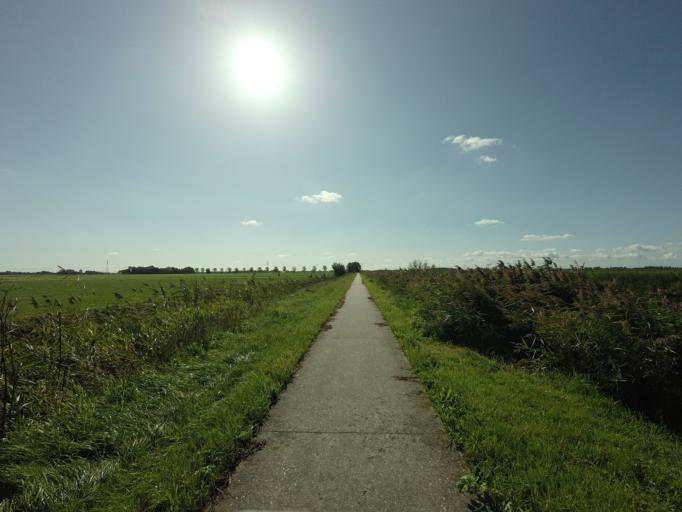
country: NL
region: Friesland
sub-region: Gemeente Boarnsterhim
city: Reduzum
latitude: 53.1242
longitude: 5.7549
